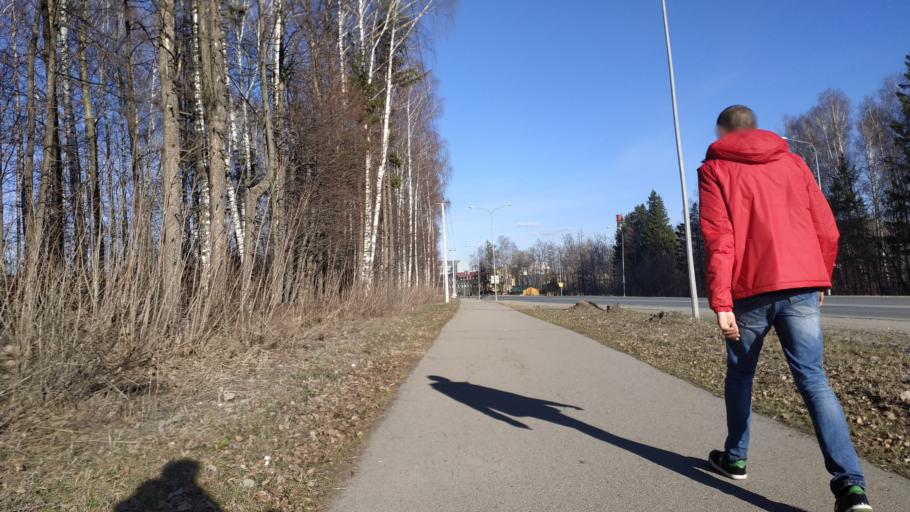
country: RU
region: Chuvashia
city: Novyye Lapsary
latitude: 56.1299
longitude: 47.1569
